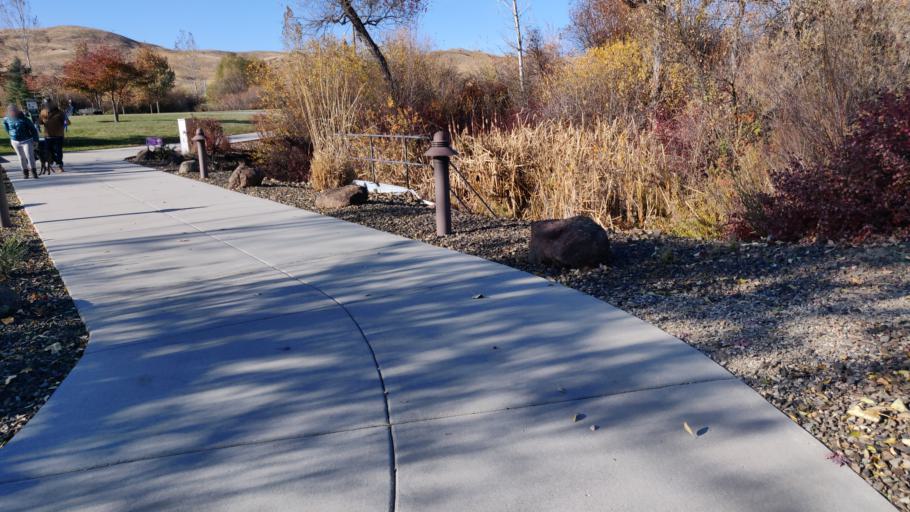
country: US
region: Idaho
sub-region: Ada County
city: Eagle
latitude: 43.7751
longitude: -116.2634
